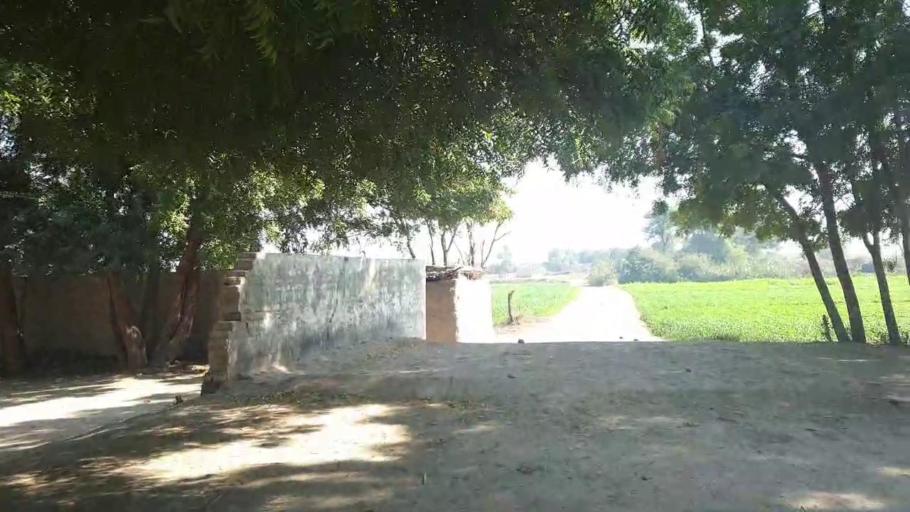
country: PK
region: Sindh
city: Shahdadpur
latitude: 25.9888
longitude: 68.5173
